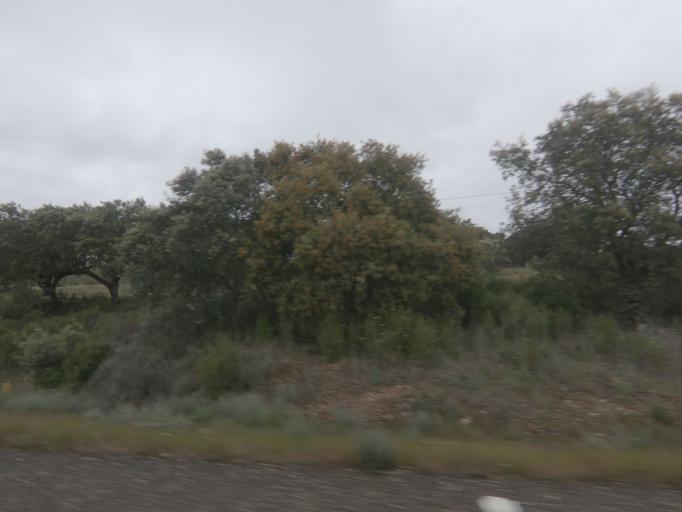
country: ES
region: Extremadura
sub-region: Provincia de Badajoz
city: La Roca de la Sierra
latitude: 39.1225
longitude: -6.6719
